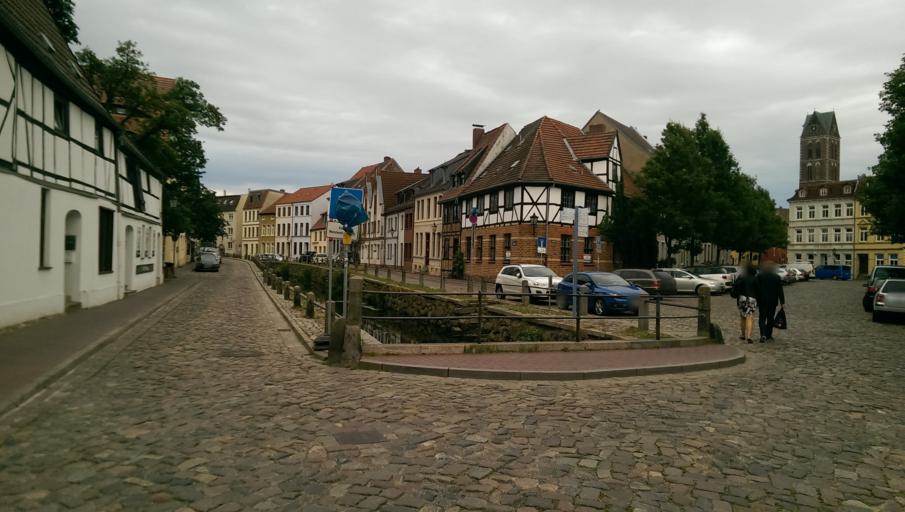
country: DE
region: Mecklenburg-Vorpommern
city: Wismar
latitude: 53.8947
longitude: 11.4613
